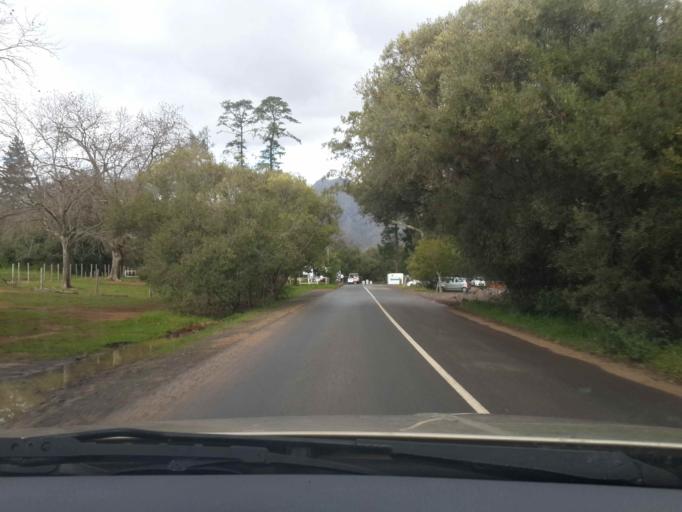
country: ZA
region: Western Cape
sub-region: Cape Winelands District Municipality
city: Stellenbosch
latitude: -33.9680
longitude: 18.9340
